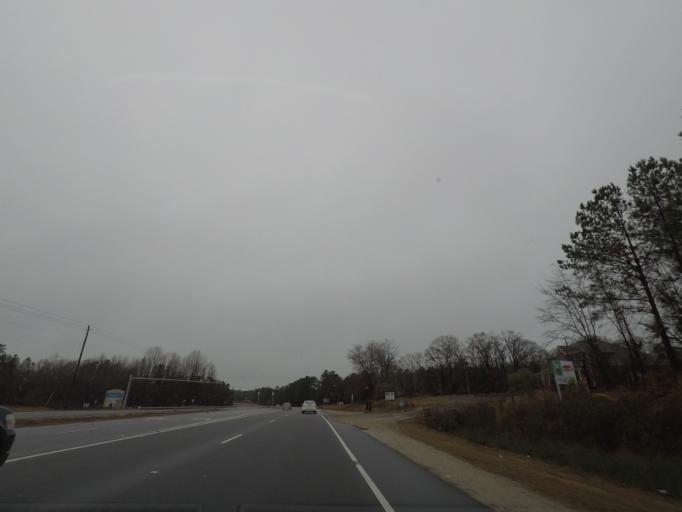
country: US
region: North Carolina
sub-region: Cumberland County
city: Spring Lake
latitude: 35.2456
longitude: -79.0228
